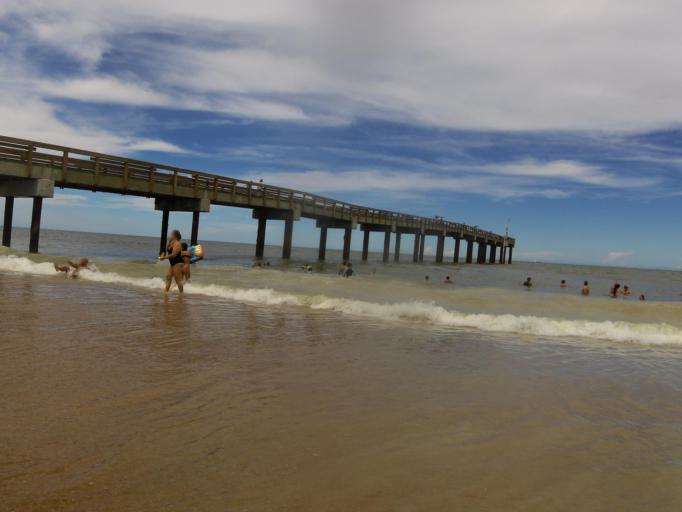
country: US
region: Florida
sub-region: Saint Johns County
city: Saint Augustine Beach
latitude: 29.8569
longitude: -81.2652
